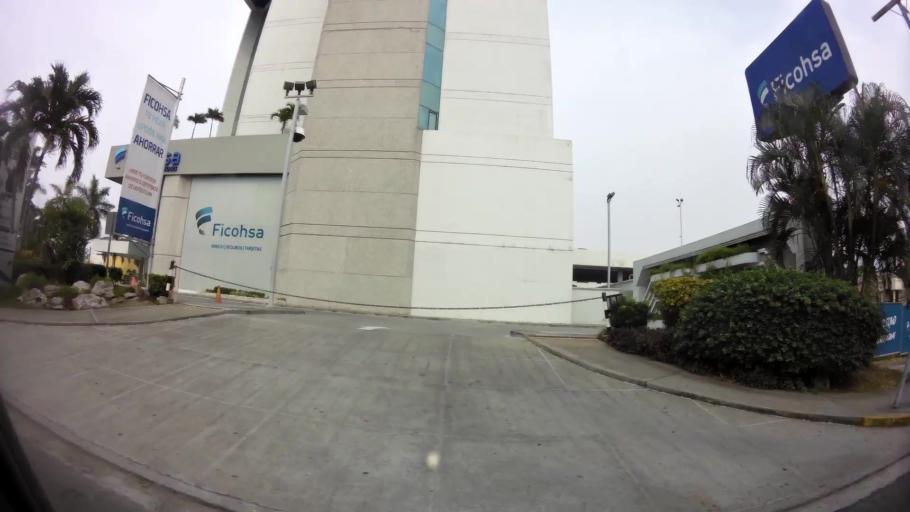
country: HN
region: Cortes
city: San Pedro Sula
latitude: 15.5036
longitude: -88.0375
